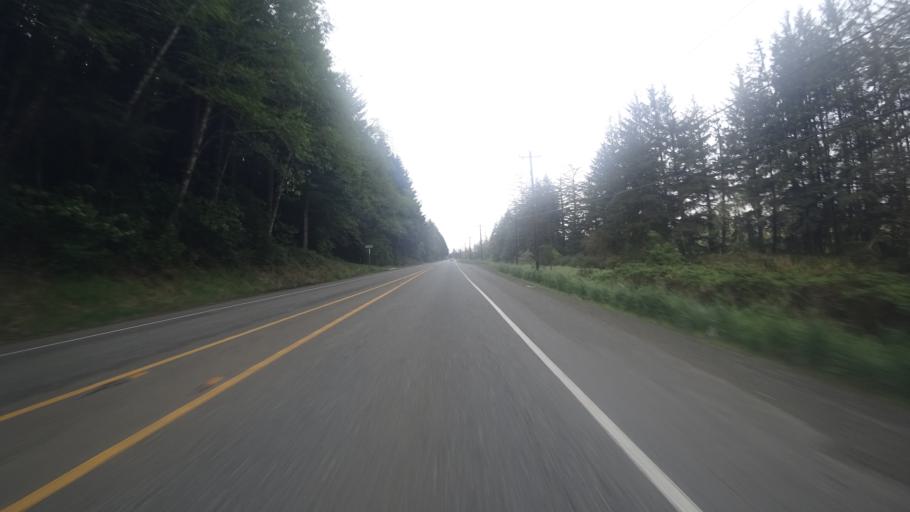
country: US
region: Oregon
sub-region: Coos County
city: North Bend
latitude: 43.4887
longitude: -124.2209
